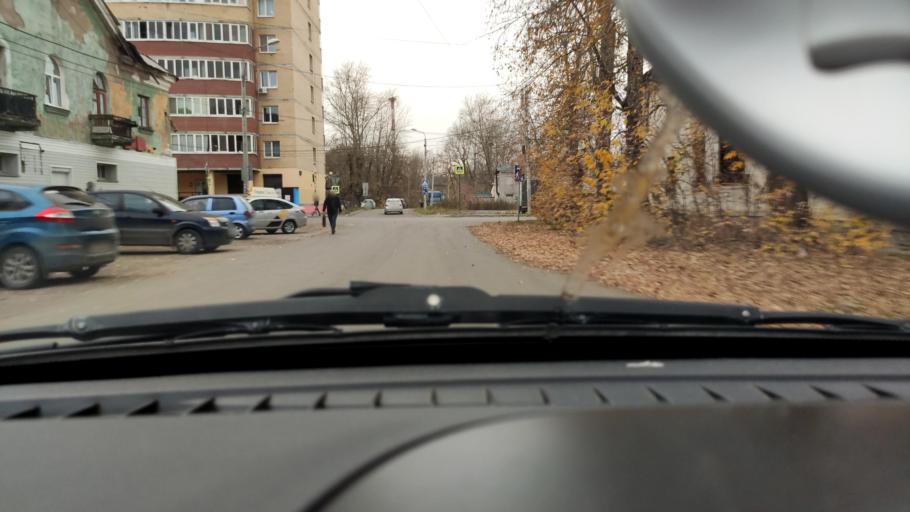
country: RU
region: Perm
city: Perm
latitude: 57.9980
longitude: 56.1815
